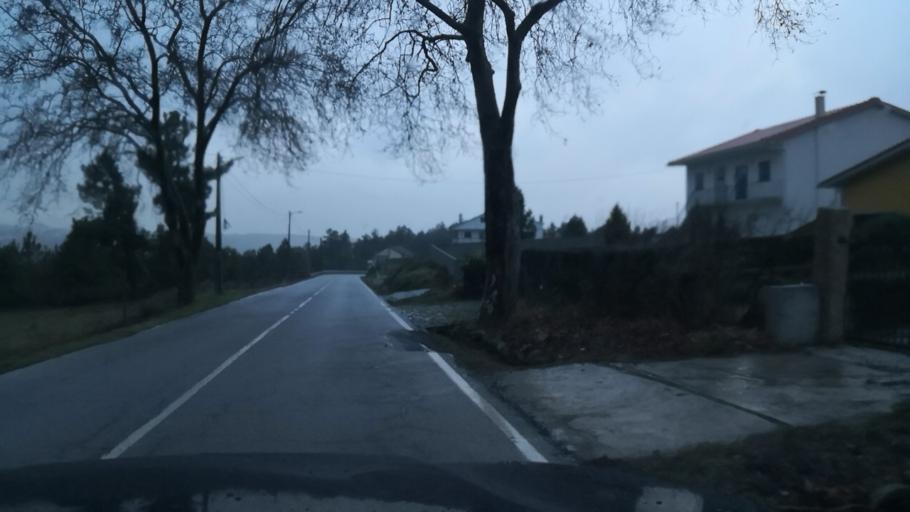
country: PT
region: Vila Real
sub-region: Murca
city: Murca
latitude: 41.3907
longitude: -7.4951
